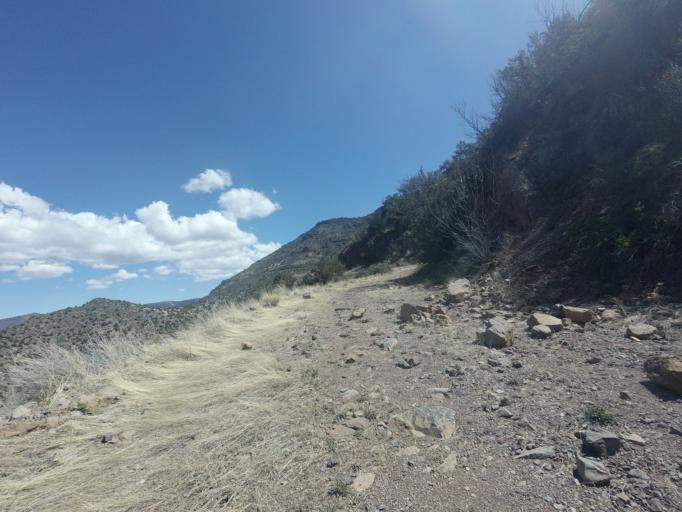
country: US
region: Arizona
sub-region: Gila County
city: Pine
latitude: 34.4029
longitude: -111.6042
